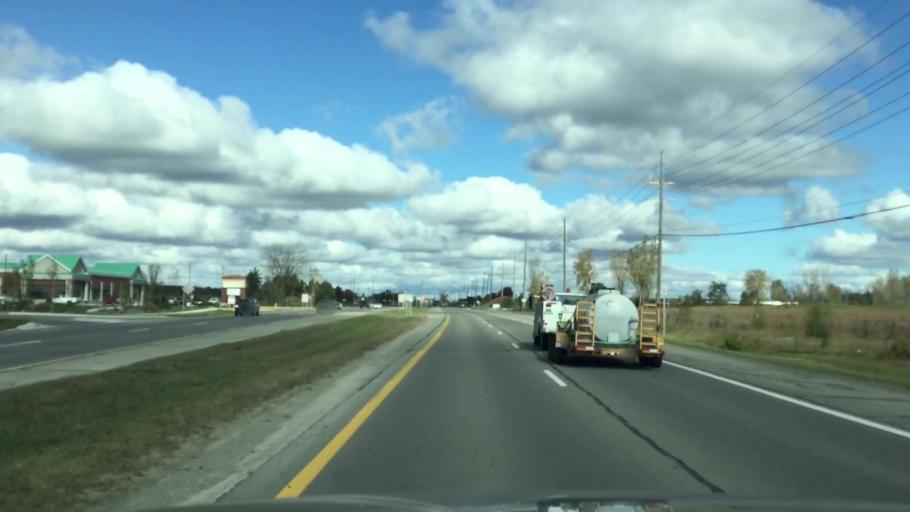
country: US
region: Michigan
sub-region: Oakland County
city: Oxford
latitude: 42.8324
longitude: -83.2702
